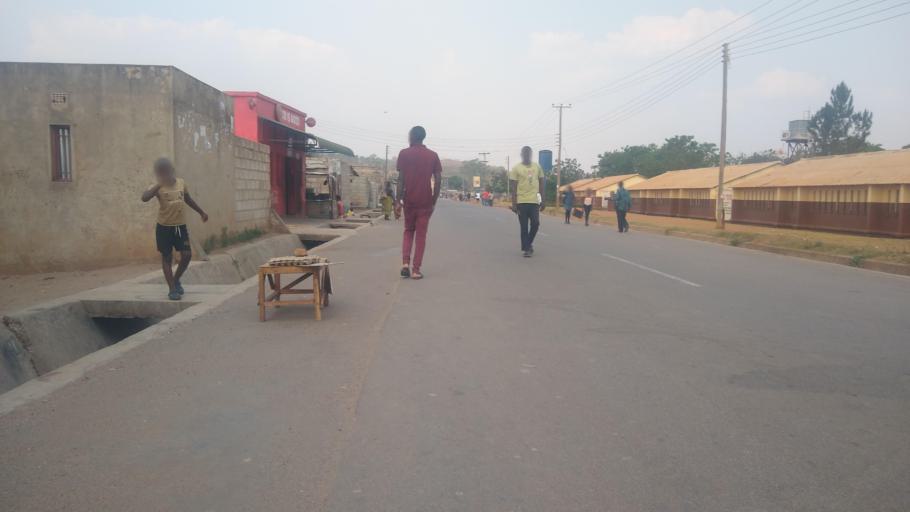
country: ZM
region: Lusaka
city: Lusaka
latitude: -15.4470
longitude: 28.3814
